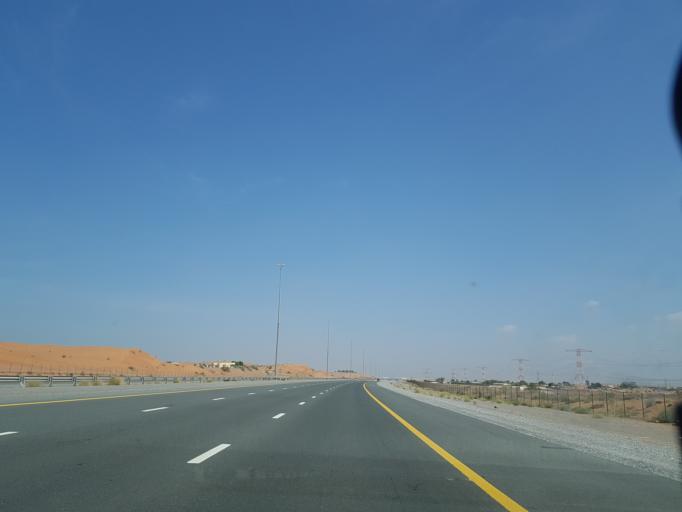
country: AE
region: Ra's al Khaymah
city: Ras al-Khaimah
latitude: 25.6783
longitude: 55.9038
